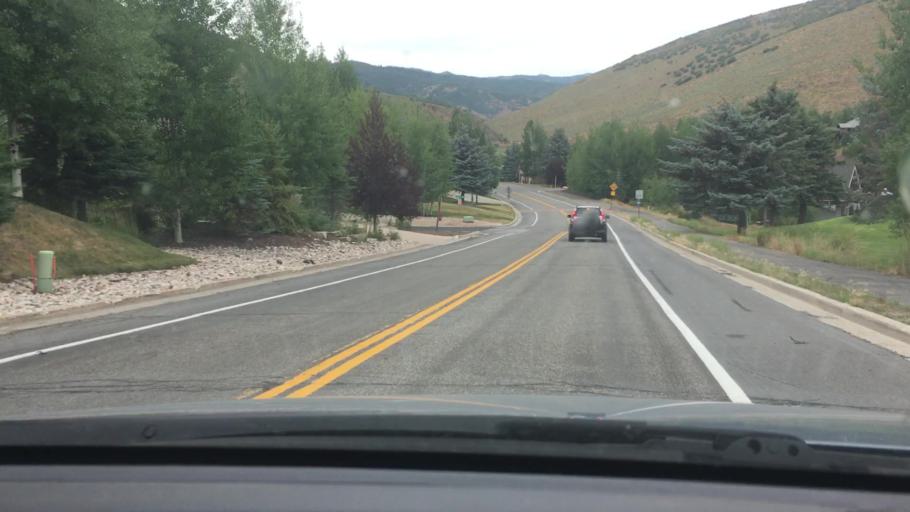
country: US
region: Utah
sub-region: Summit County
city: Summit Park
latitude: 40.7616
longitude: -111.5785
